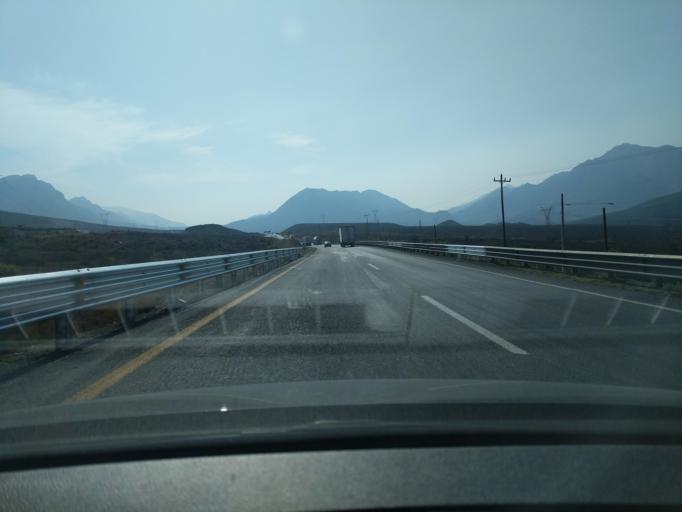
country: MX
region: Nuevo Leon
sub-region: Garcia
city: Las Torres de Guadalupe
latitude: 25.6790
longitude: -100.6673
